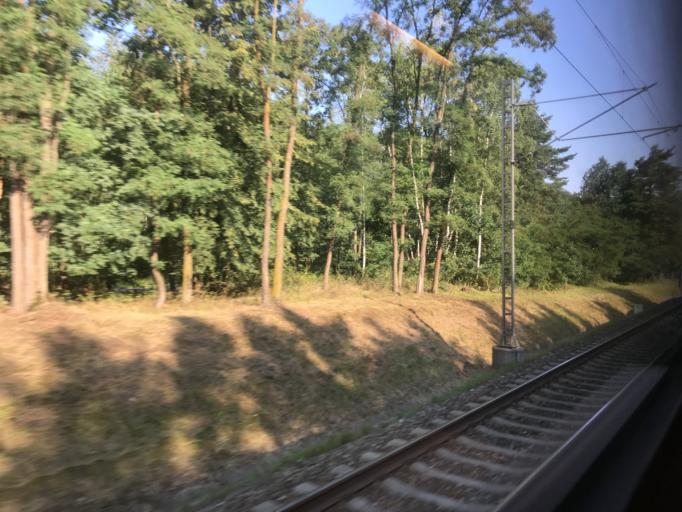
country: CZ
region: Jihocesky
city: Plana nad Luznici
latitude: 49.3322
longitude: 14.7141
